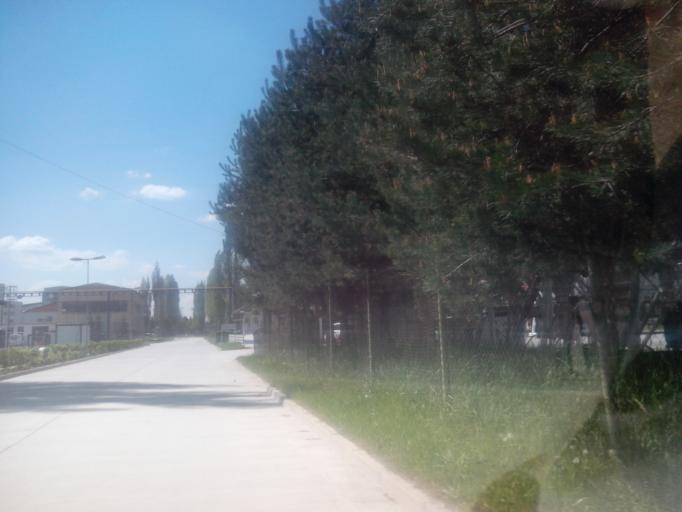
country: CZ
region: Central Bohemia
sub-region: Okres Beroun
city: Kraluv Dvur
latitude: 49.9514
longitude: 14.0542
